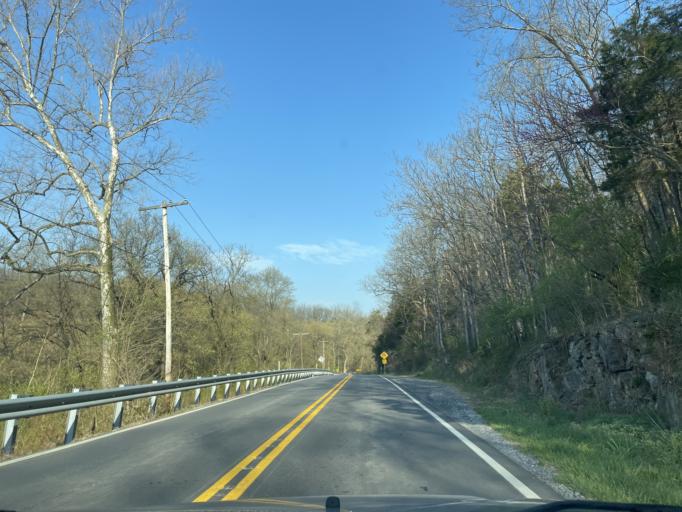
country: US
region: Maryland
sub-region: Washington County
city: Keedysville
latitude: 39.5352
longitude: -77.7099
